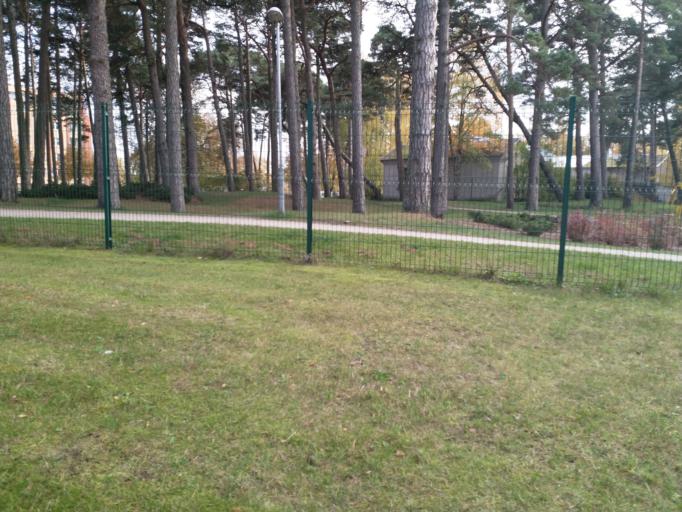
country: LV
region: Ventspils
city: Ventspils
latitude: 57.4072
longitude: 21.5918
